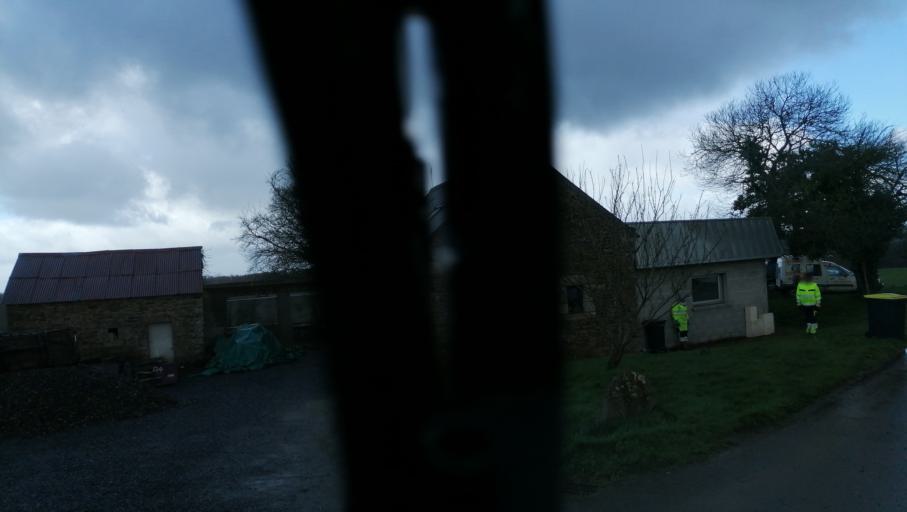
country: FR
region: Brittany
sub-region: Departement des Cotes-d'Armor
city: Lanrodec
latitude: 48.4891
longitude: -3.0335
